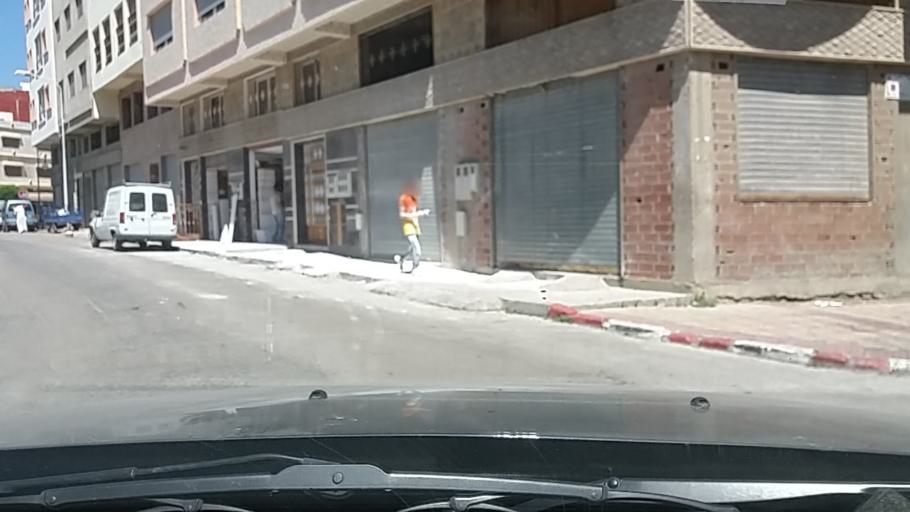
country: MA
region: Tanger-Tetouan
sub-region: Tanger-Assilah
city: Tangier
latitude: 35.7529
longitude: -5.7992
